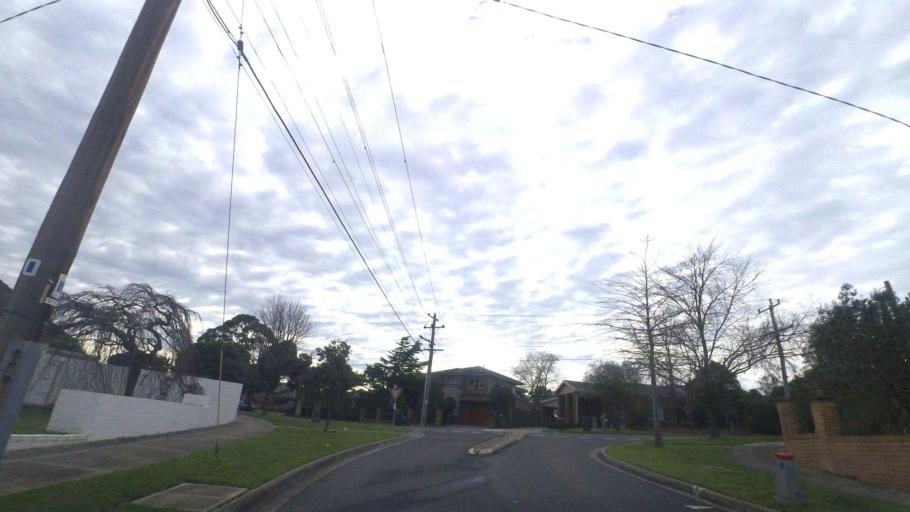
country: AU
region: Victoria
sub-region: Manningham
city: Templestowe Lower
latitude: -37.7680
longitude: 145.1083
